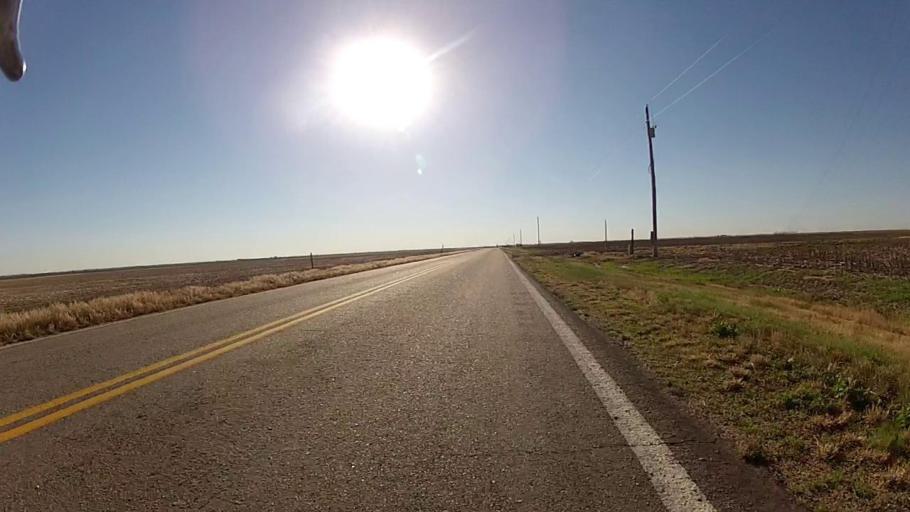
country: US
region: Kansas
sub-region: Ford County
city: Dodge City
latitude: 37.6463
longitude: -99.8397
